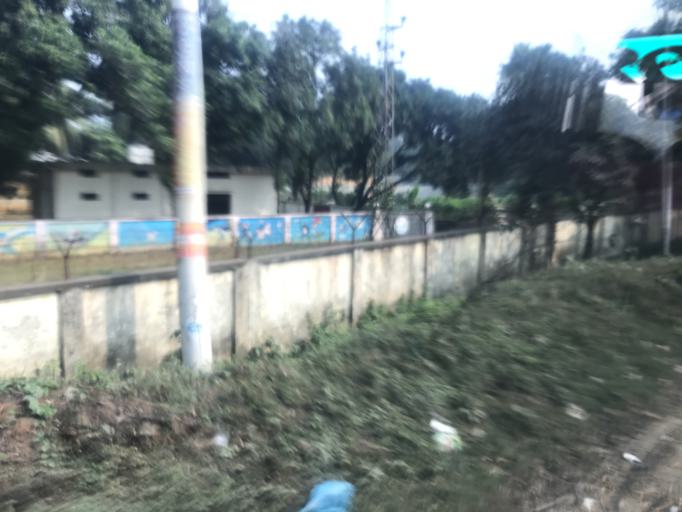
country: BD
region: Dhaka
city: Tungi
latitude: 23.9083
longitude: 90.2649
